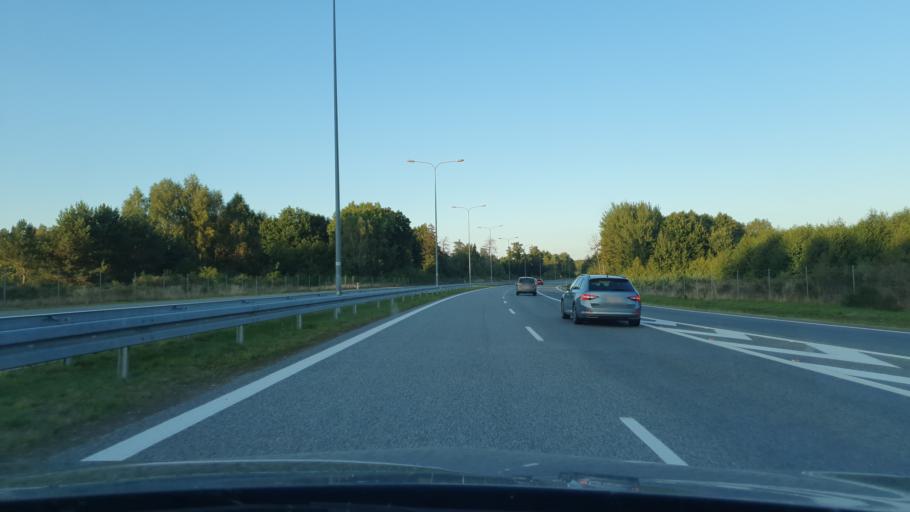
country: PL
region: Pomeranian Voivodeship
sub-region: Slupsk
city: Slupsk
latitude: 54.4525
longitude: 17.0834
